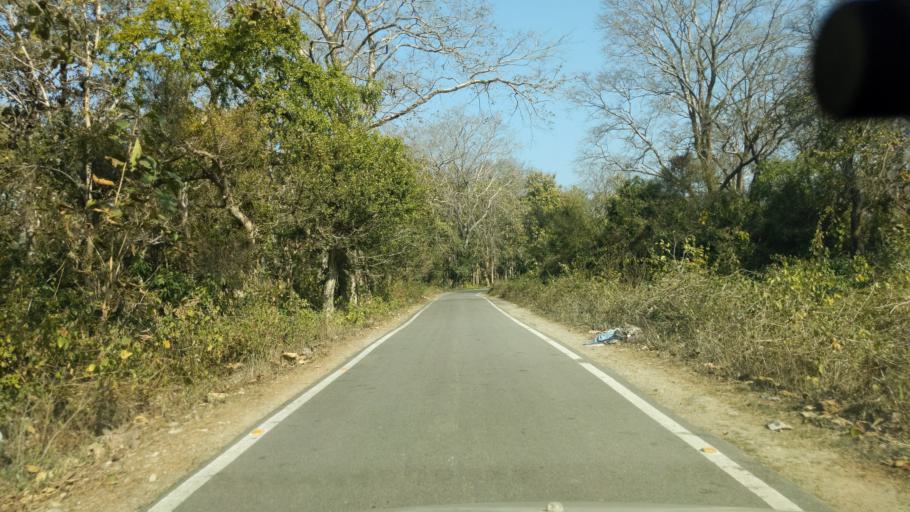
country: IN
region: Uttarakhand
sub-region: Naini Tal
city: Ramnagar
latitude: 29.4157
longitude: 79.1369
